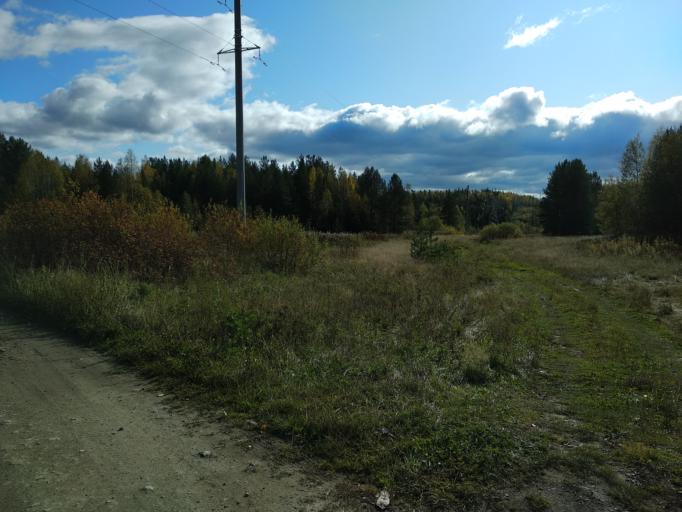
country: RU
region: Sverdlovsk
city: Krasnotur'insk
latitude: 59.9830
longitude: 60.4005
